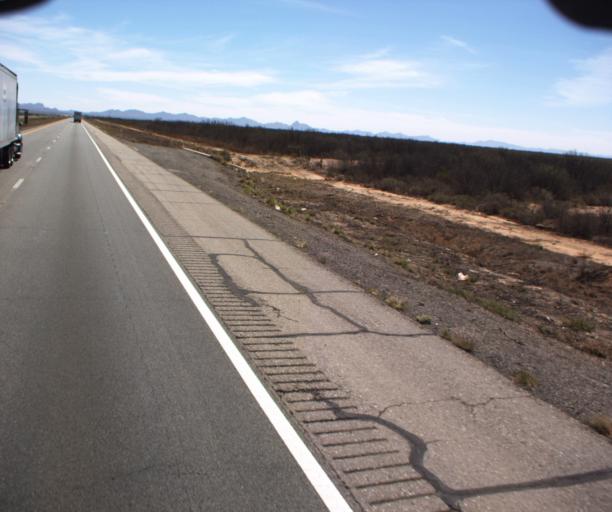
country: US
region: Arizona
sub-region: Cochise County
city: Willcox
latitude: 32.2820
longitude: -109.2877
